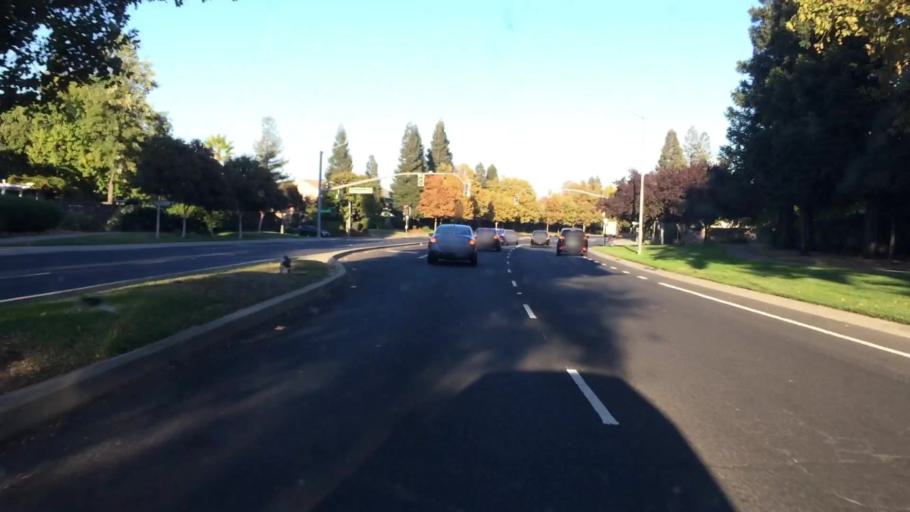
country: US
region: California
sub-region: Sacramento County
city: Laguna
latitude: 38.4352
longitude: -121.4403
